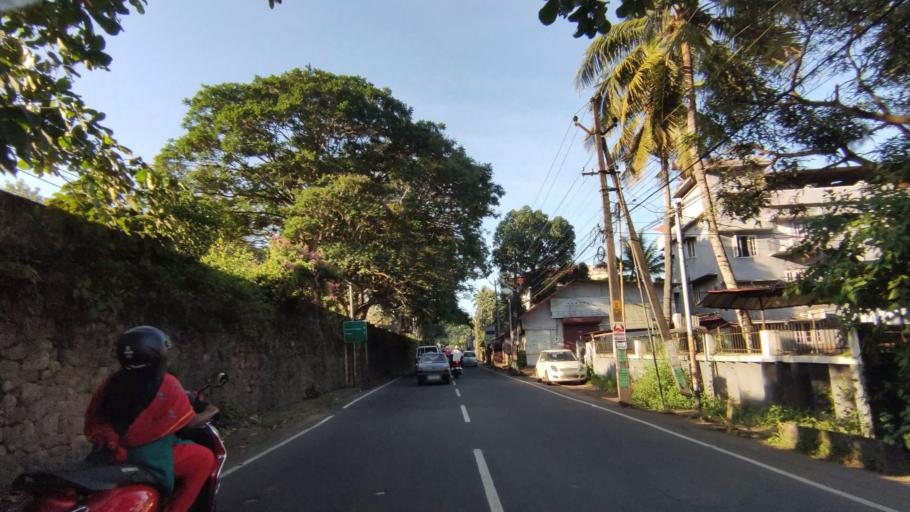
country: IN
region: Kerala
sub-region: Kottayam
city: Kottayam
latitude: 9.5981
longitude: 76.5172
